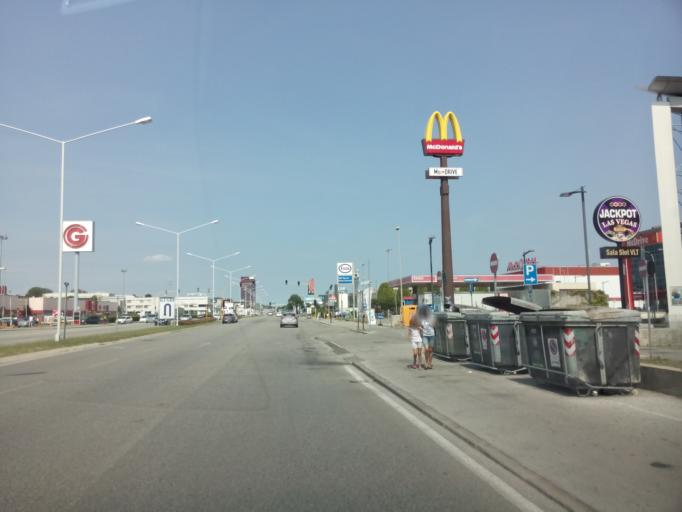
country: IT
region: Veneto
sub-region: Provincia di Padova
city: Padova
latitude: 45.4102
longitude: 11.9062
